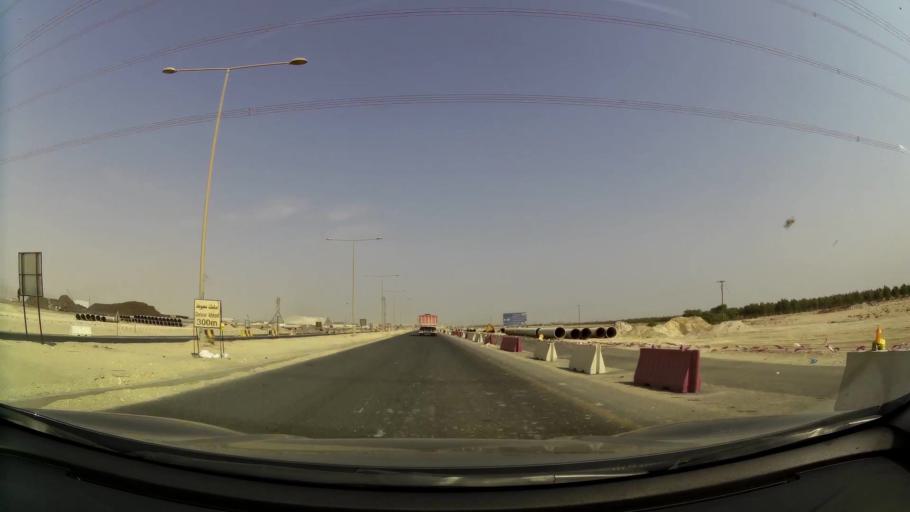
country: KW
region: Al Ahmadi
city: Al Fahahil
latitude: 28.9652
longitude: 48.1253
